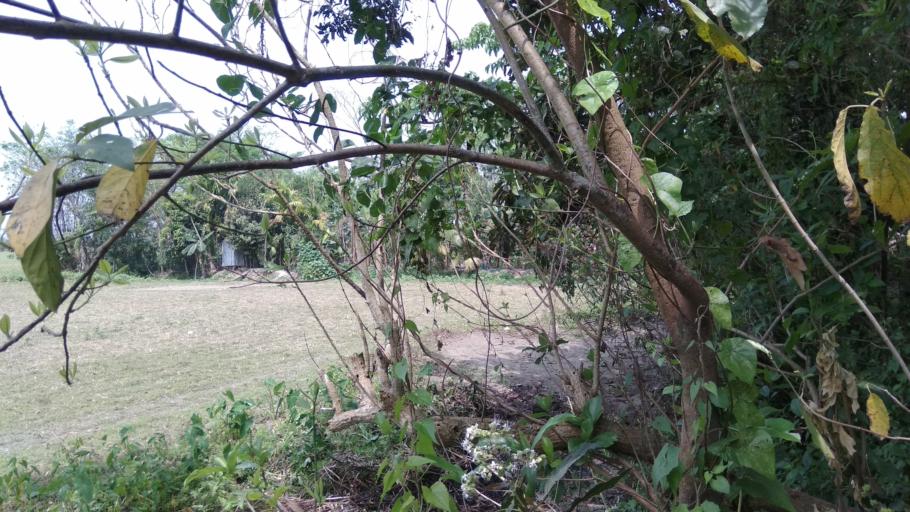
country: BD
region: Barisal
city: Mehendiganj
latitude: 22.9217
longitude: 90.3900
